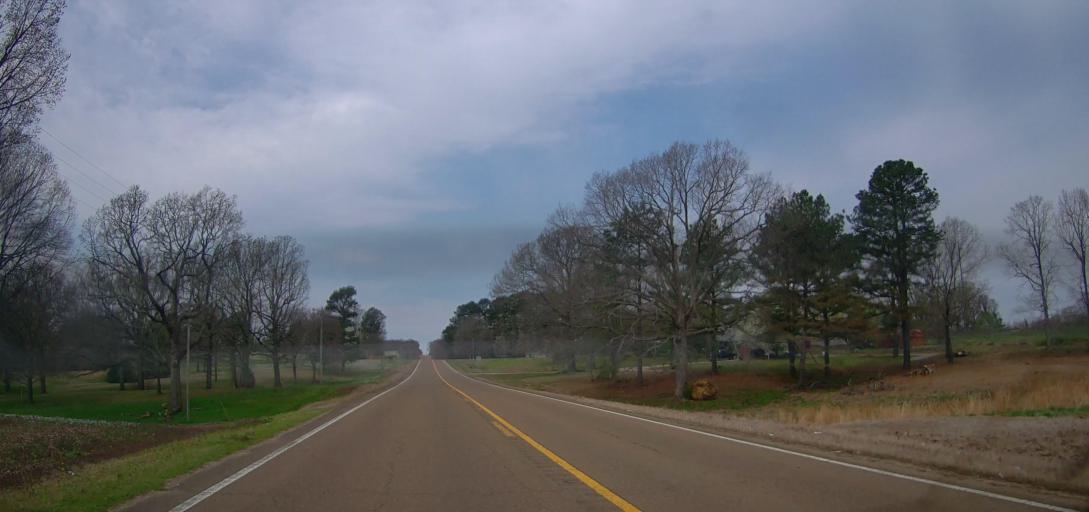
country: US
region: Mississippi
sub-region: Marshall County
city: Byhalia
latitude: 34.8319
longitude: -89.5759
